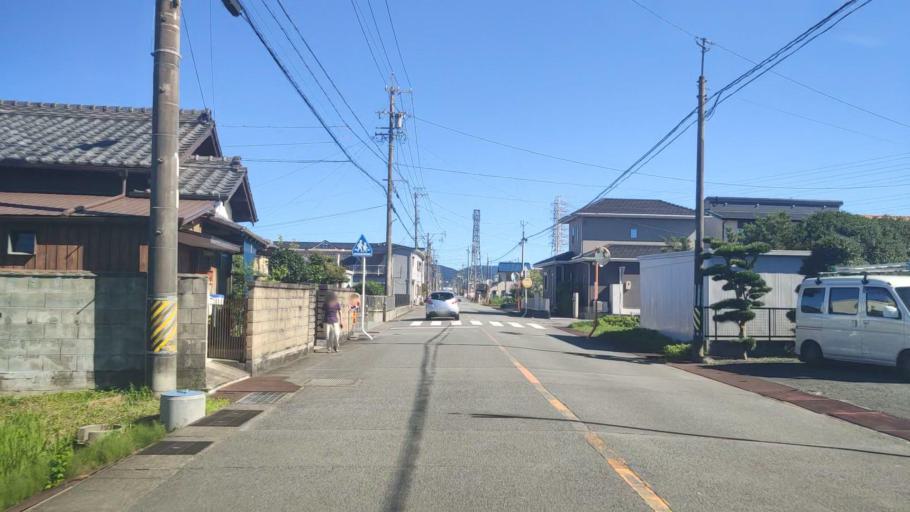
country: JP
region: Mie
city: Ise
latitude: 34.5110
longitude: 136.7164
